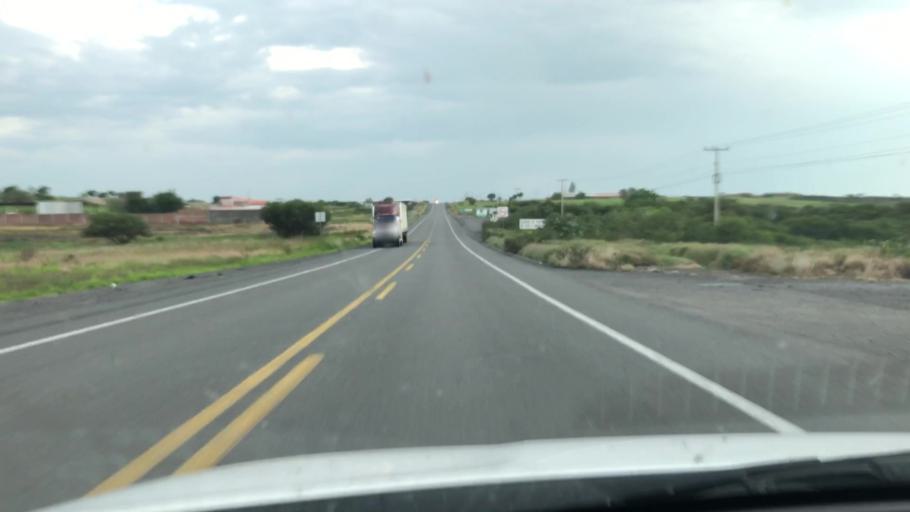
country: MX
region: Jalisco
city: Degollado
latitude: 20.3560
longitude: -102.1522
